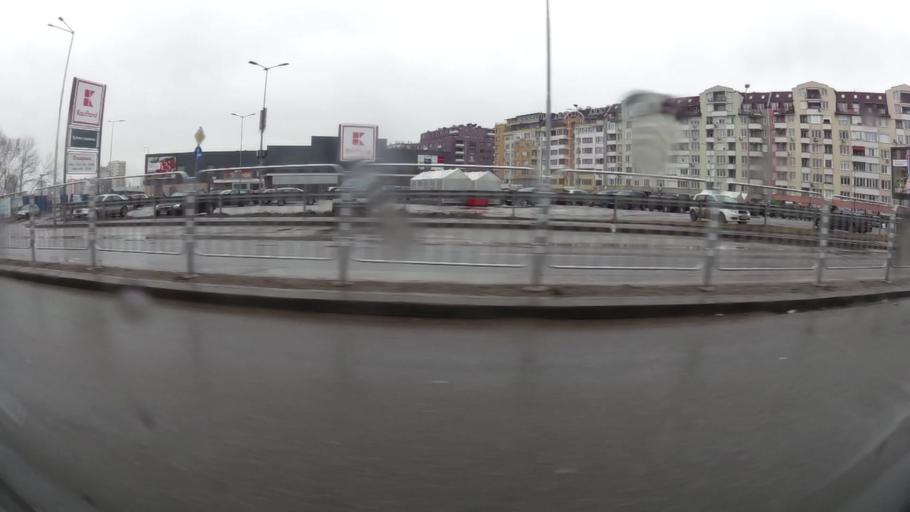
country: BG
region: Sofia-Capital
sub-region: Stolichna Obshtina
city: Sofia
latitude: 42.6449
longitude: 23.3784
